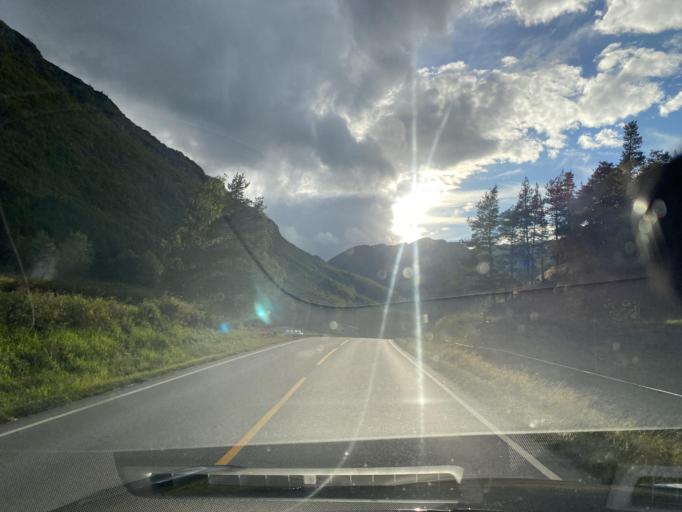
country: NO
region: Oppland
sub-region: Lom
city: Fossbergom
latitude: 61.8124
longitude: 8.4988
